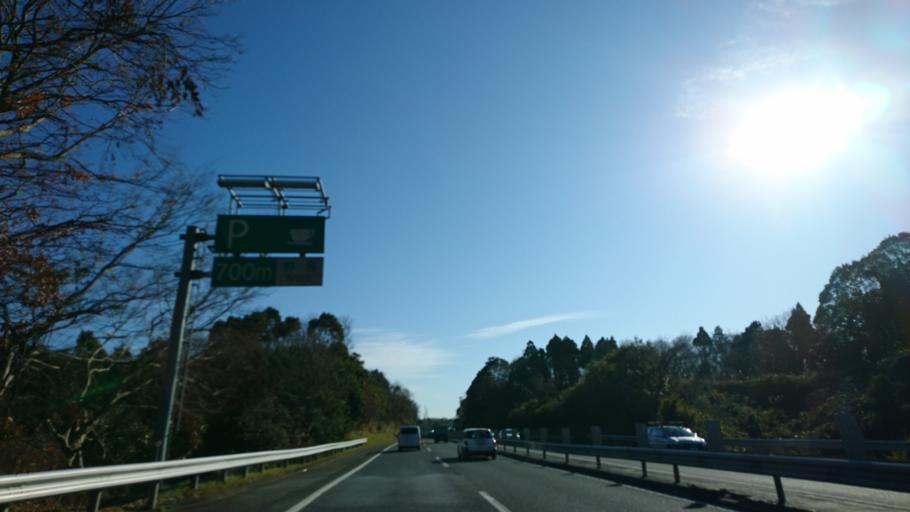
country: JP
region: Chiba
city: Yotsukaido
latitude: 35.5716
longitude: 140.2251
